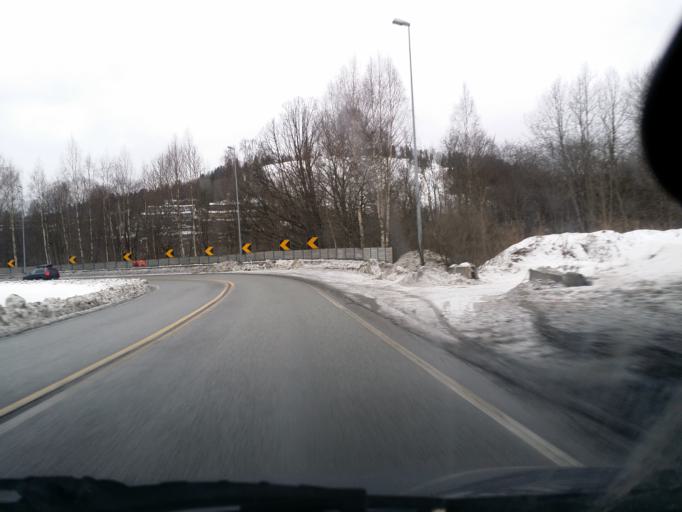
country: NO
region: Akershus
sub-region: Asker
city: Billingstad
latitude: 59.9073
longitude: 10.4860
